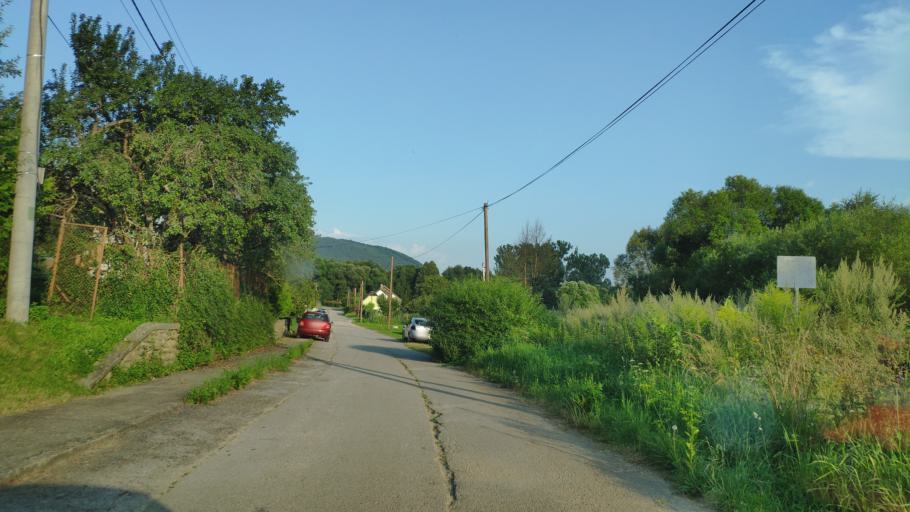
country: SK
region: Kosicky
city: Dobsina
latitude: 48.7202
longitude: 20.2748
